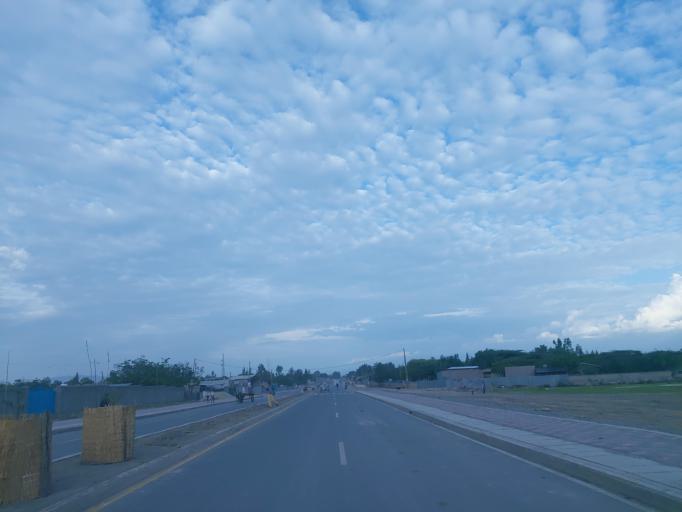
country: ET
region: Oromiya
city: Ziway
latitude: 8.1463
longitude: 38.8047
